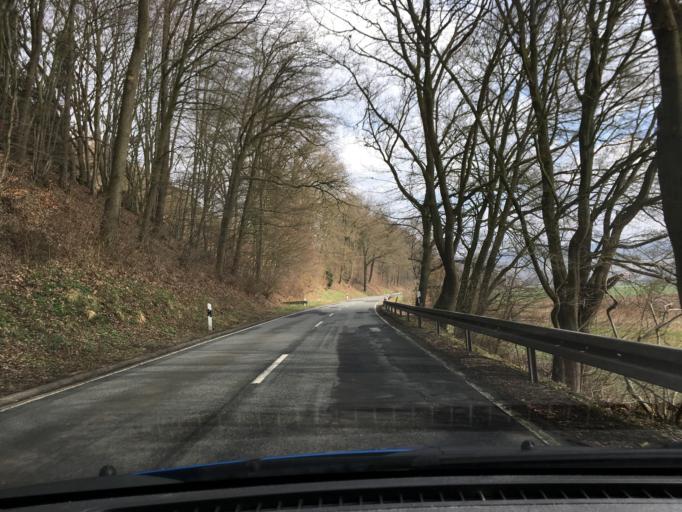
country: DE
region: Lower Saxony
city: Bodenfelde
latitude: 51.6002
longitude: 9.5750
